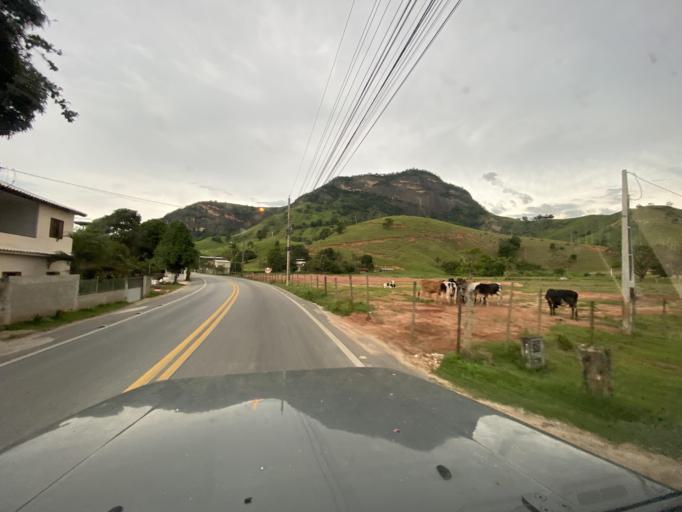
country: BR
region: Espirito Santo
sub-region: Jeronimo Monteiro
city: Jeronimo Monteiro
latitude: -20.8035
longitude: -41.3596
